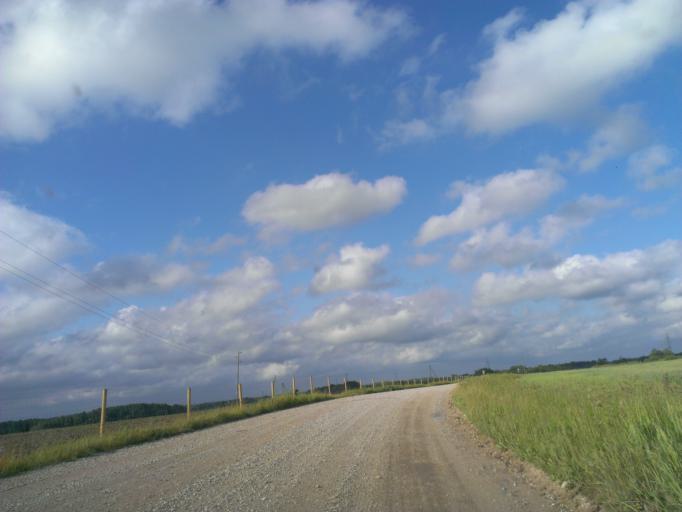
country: LV
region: Aizpute
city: Aizpute
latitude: 56.7709
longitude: 21.4703
